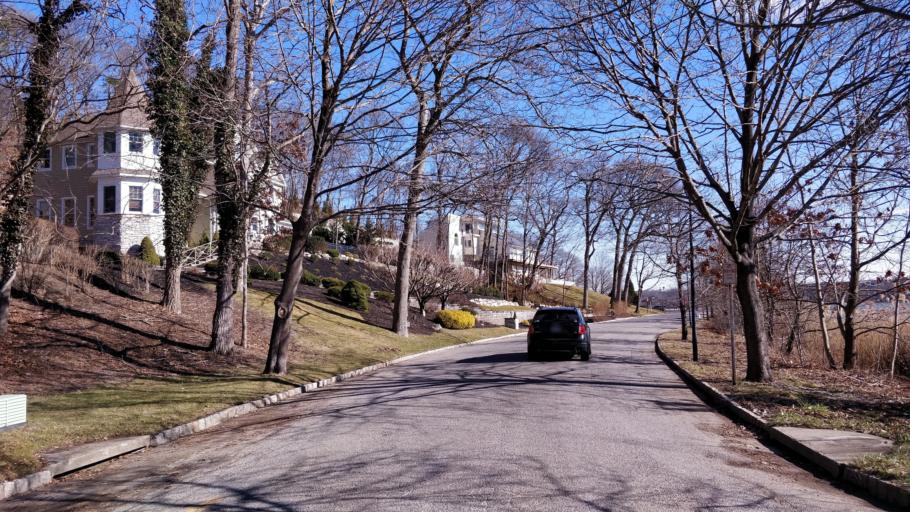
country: US
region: New York
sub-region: Suffolk County
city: Mount Sinai
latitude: 40.9576
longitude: -73.0437
